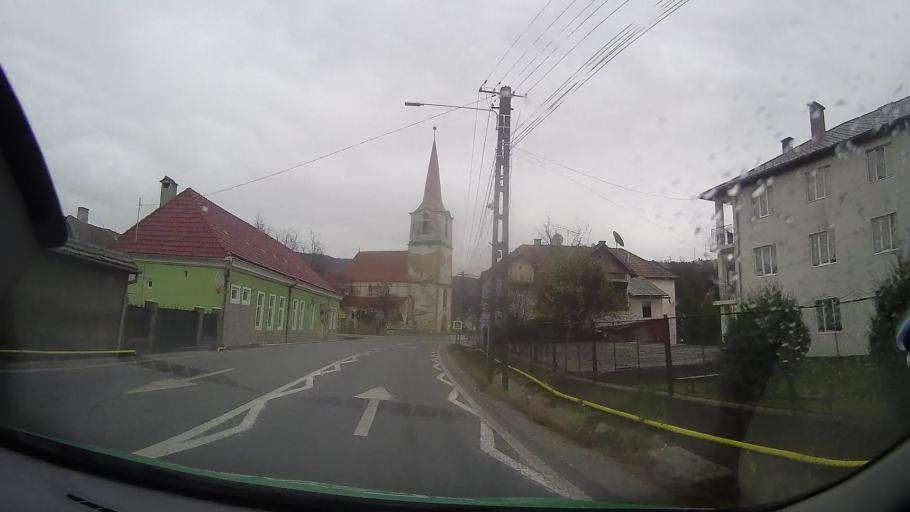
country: RO
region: Bistrita-Nasaud
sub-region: Comuna Teaca
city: Teaca
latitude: 46.9116
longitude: 24.5059
